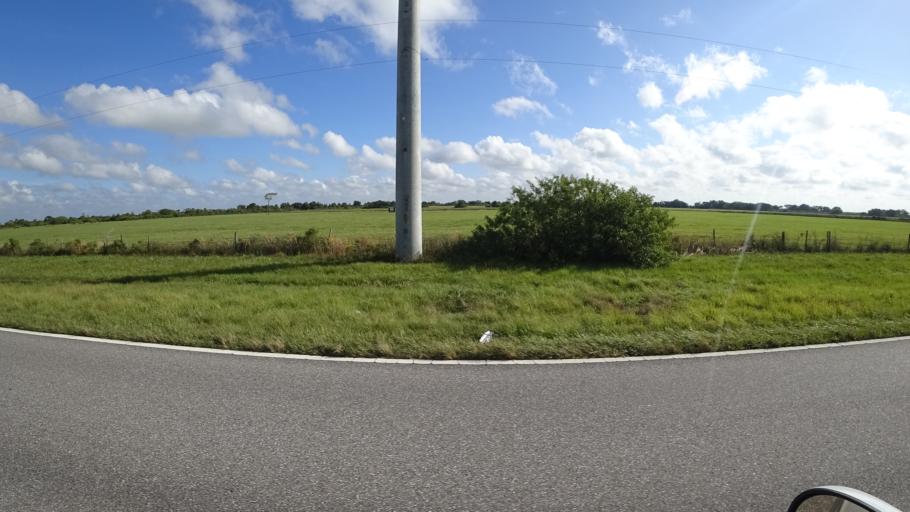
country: US
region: Florida
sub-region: Hillsborough County
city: Wimauma
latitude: 27.5174
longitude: -82.3262
